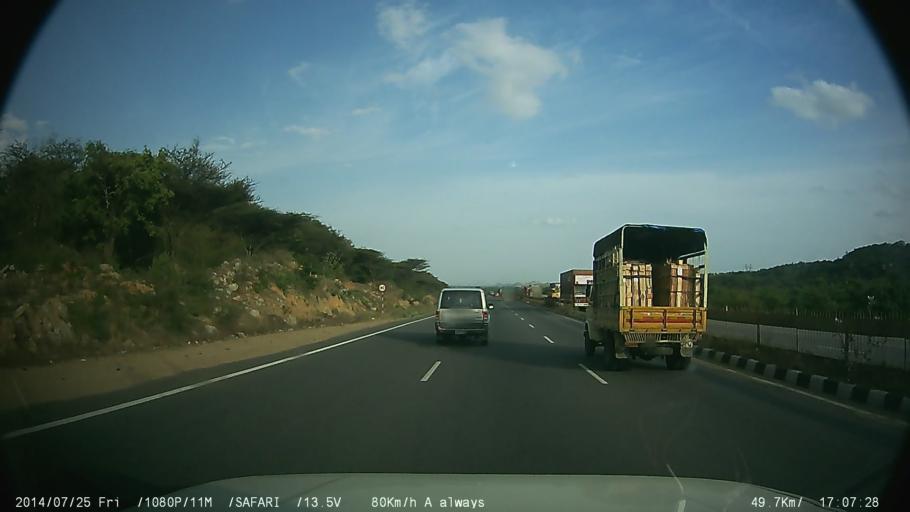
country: IN
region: Tamil Nadu
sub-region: Krishnagiri
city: Hosur
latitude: 12.6958
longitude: 77.9153
